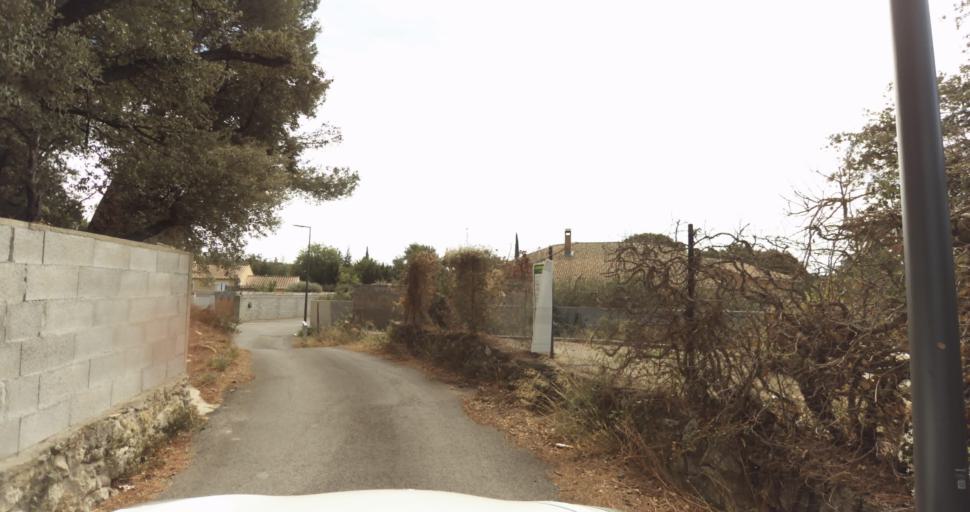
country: FR
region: Provence-Alpes-Cote d'Azur
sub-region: Departement des Bouches-du-Rhone
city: Miramas
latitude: 43.5783
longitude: 5.0248
